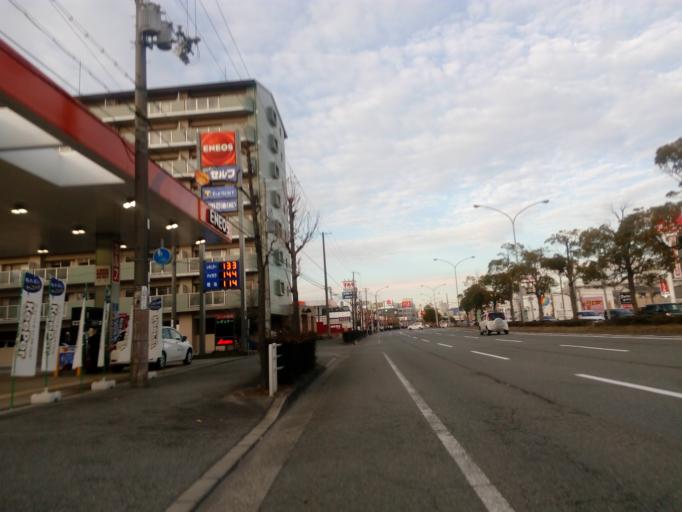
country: JP
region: Hyogo
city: Himeji
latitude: 34.8066
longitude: 134.6803
